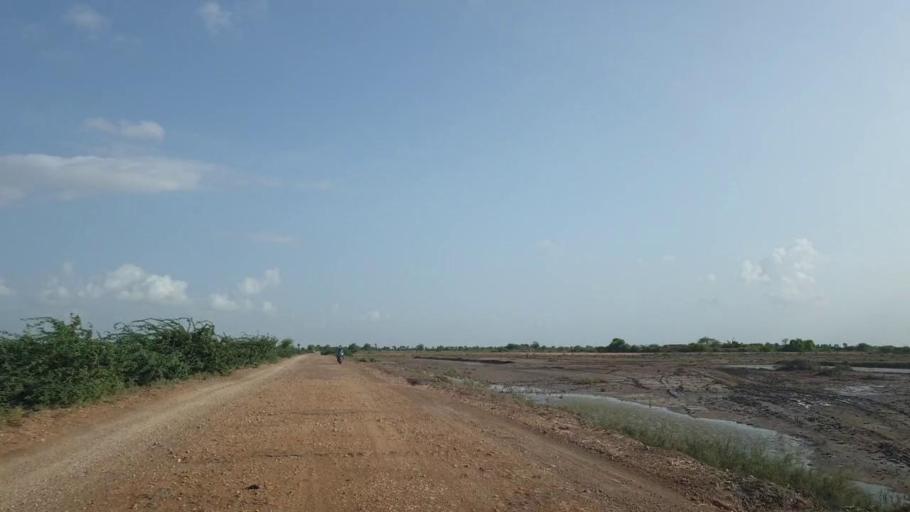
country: PK
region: Sindh
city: Kadhan
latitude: 24.6359
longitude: 69.0960
